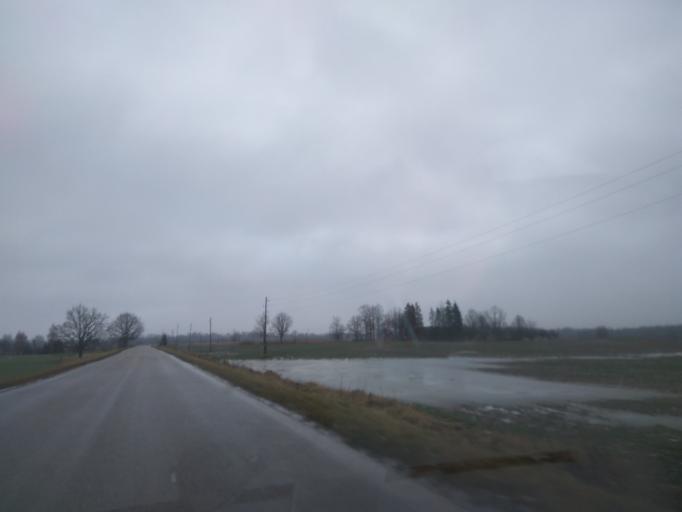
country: LV
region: Saldus Rajons
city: Saldus
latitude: 56.8407
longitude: 22.3793
